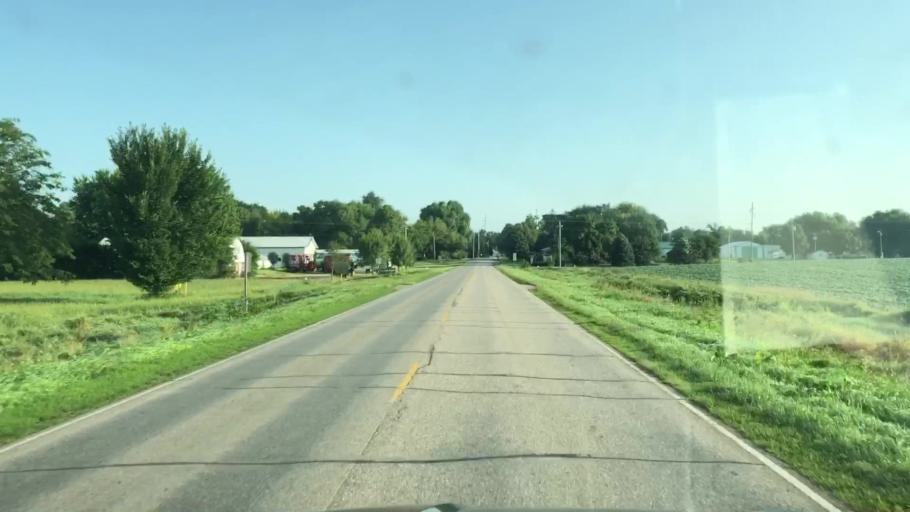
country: US
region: Iowa
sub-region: Lyon County
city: George
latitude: 43.3367
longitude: -95.9987
